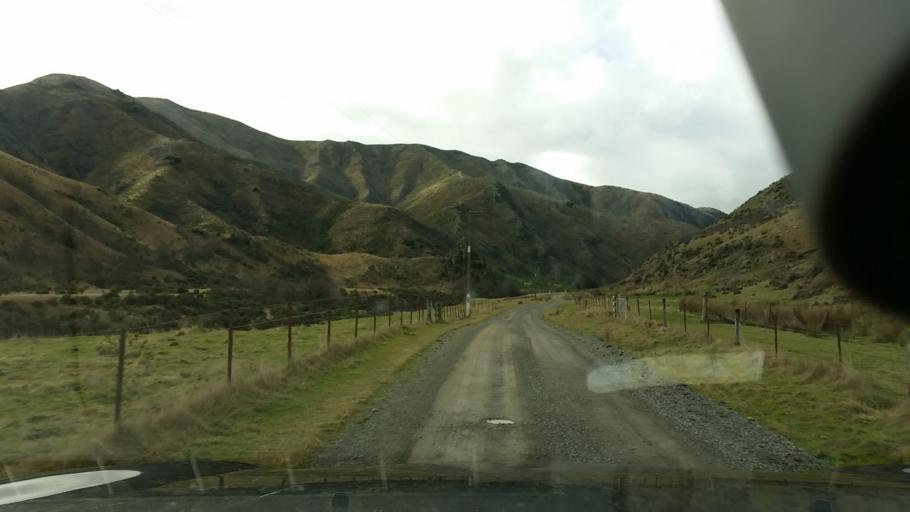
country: NZ
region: Tasman
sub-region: Tasman District
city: Richmond
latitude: -41.7337
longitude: 173.4326
